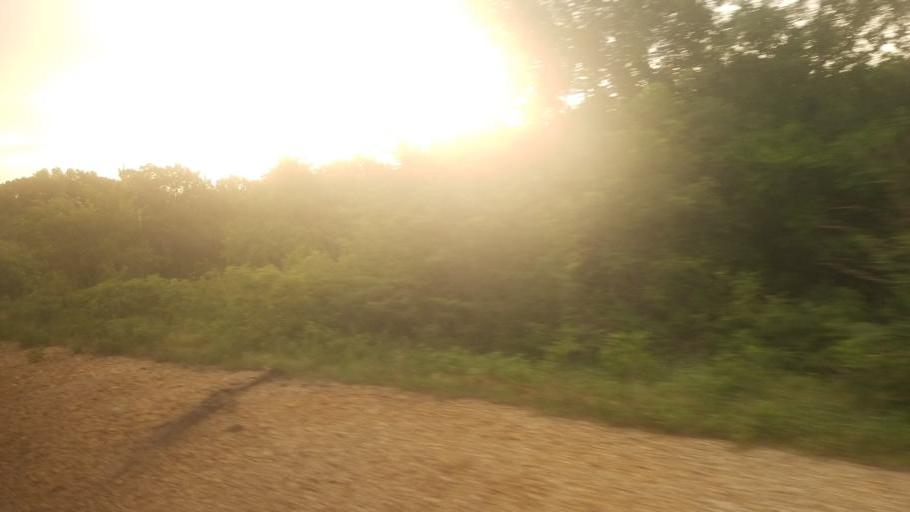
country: US
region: Kansas
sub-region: Lyon County
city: Emporia
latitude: 38.4323
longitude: -96.1194
